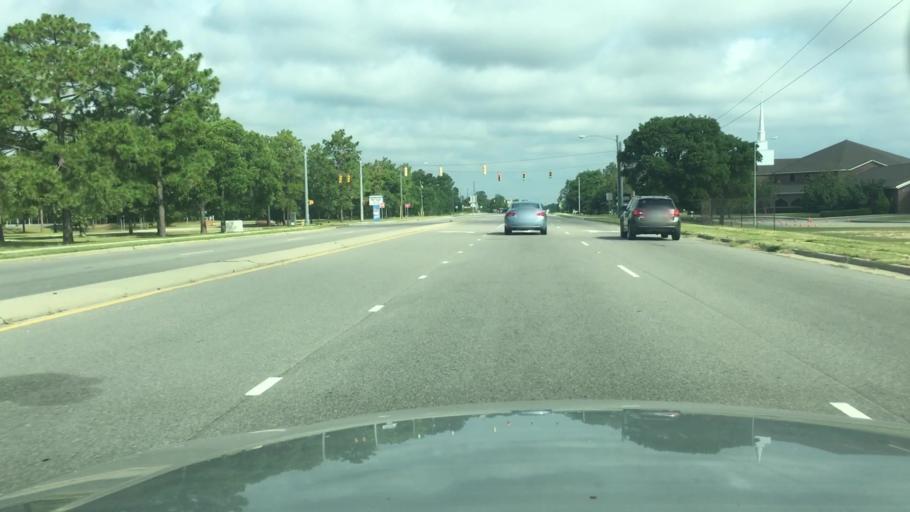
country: US
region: North Carolina
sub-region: Cumberland County
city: Hope Mills
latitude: 34.9808
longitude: -78.9273
